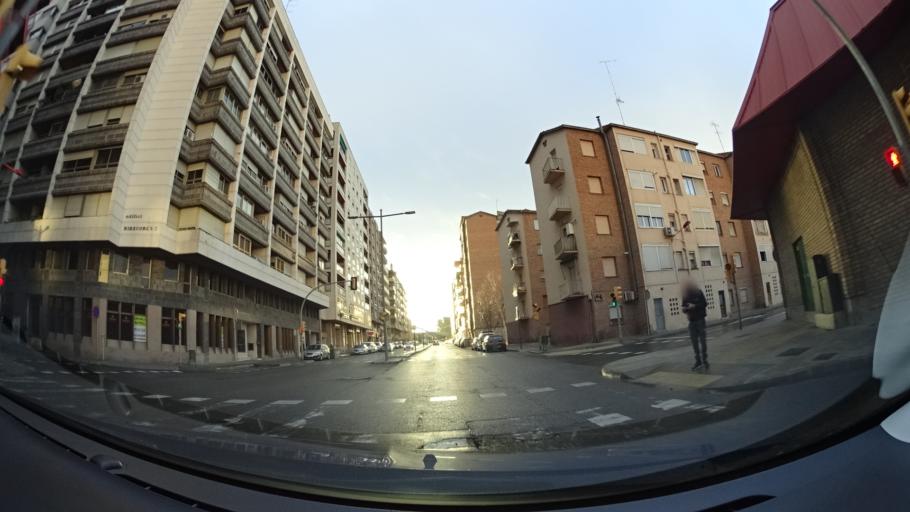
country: ES
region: Catalonia
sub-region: Provincia de Lleida
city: Lleida
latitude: 41.6096
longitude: 0.6202
